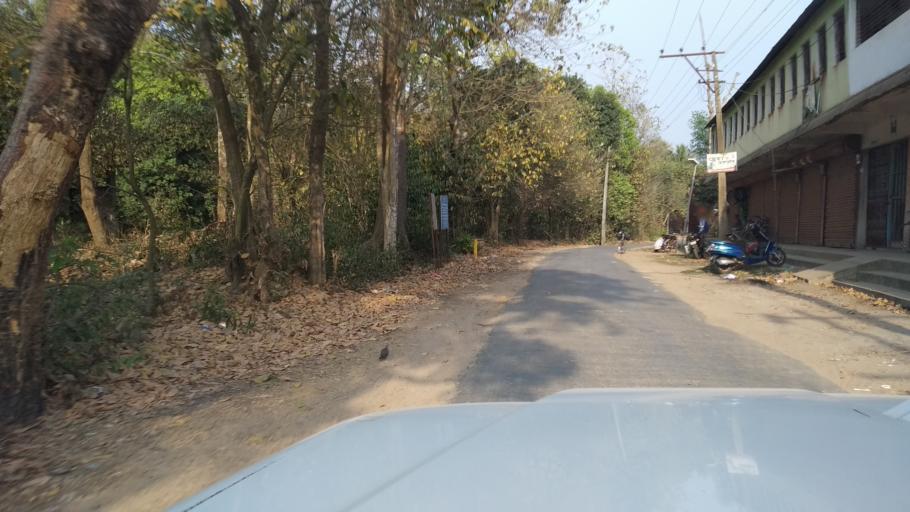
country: IN
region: Tripura
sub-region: West Tripura
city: Sonamura
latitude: 23.4190
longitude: 91.2811
